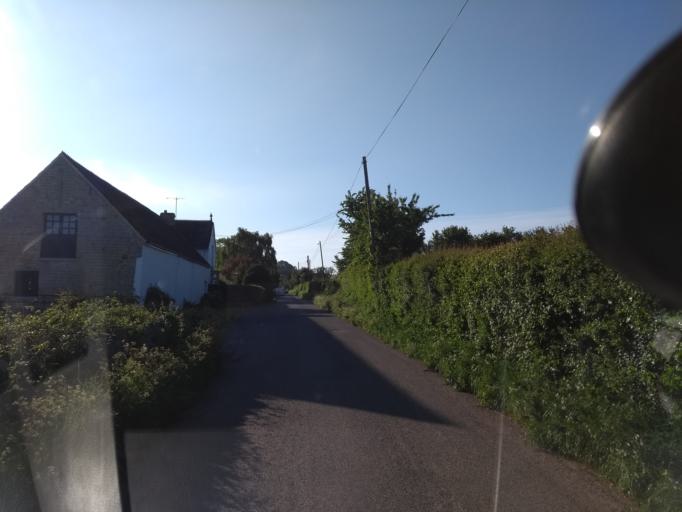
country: GB
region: England
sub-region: Somerset
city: Creech Saint Michael
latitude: 50.9963
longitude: -3.0555
